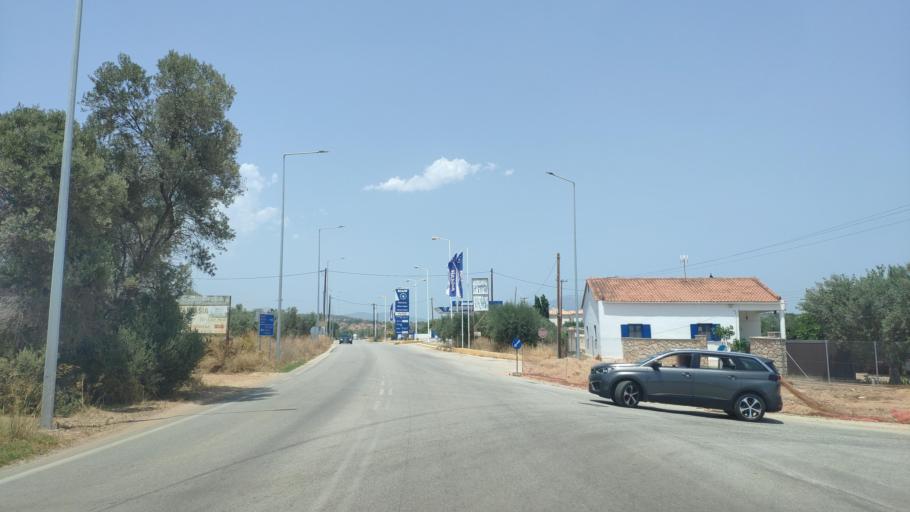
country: GR
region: Peloponnese
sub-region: Nomos Argolidos
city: Porto Cheli
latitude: 37.3427
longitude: 23.1576
